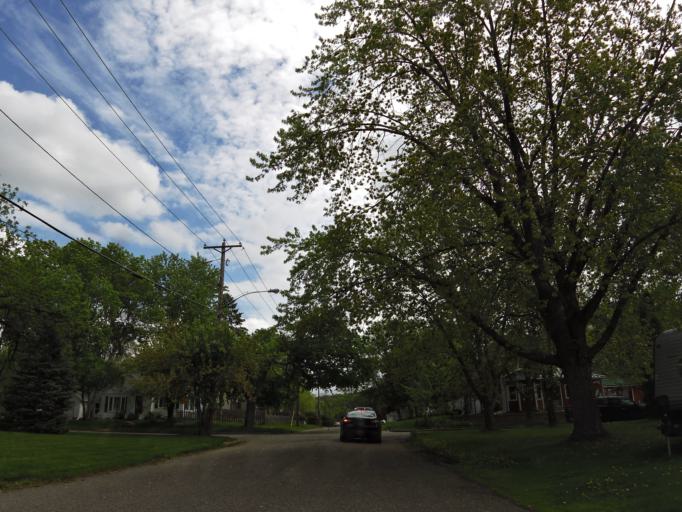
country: US
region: Wisconsin
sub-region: Saint Croix County
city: Hudson
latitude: 44.9831
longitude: -92.7484
